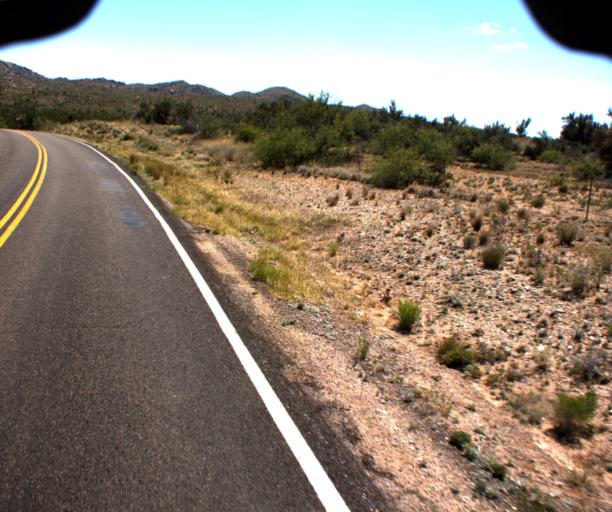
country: US
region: Arizona
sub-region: Yavapai County
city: Bagdad
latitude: 34.5221
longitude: -113.1343
